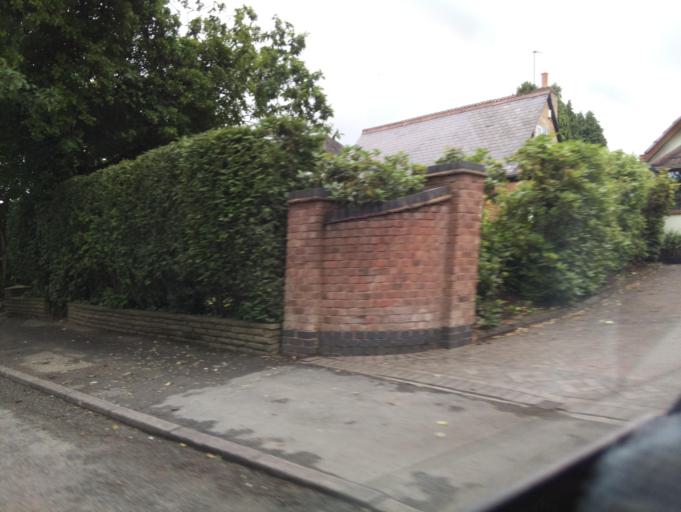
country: GB
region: England
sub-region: Solihull
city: Tidbury Green
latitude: 52.3797
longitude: -1.8570
